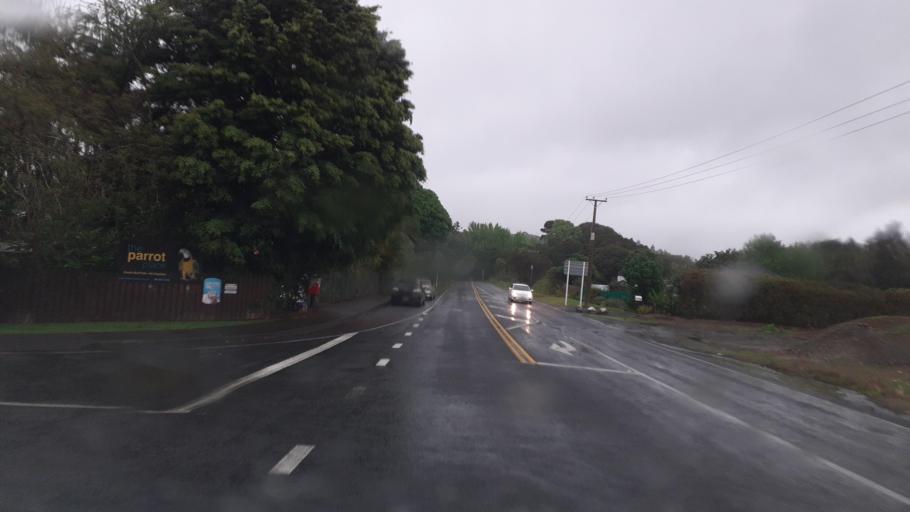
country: NZ
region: Northland
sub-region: Far North District
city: Kerikeri
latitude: -35.2114
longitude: 173.9623
